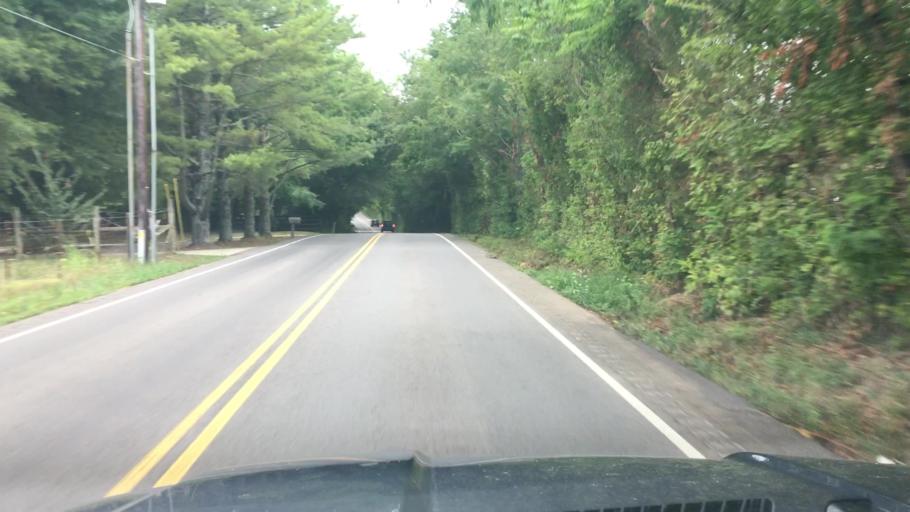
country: US
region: Tennessee
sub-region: Williamson County
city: Thompson's Station
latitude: 35.8054
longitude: -86.8626
